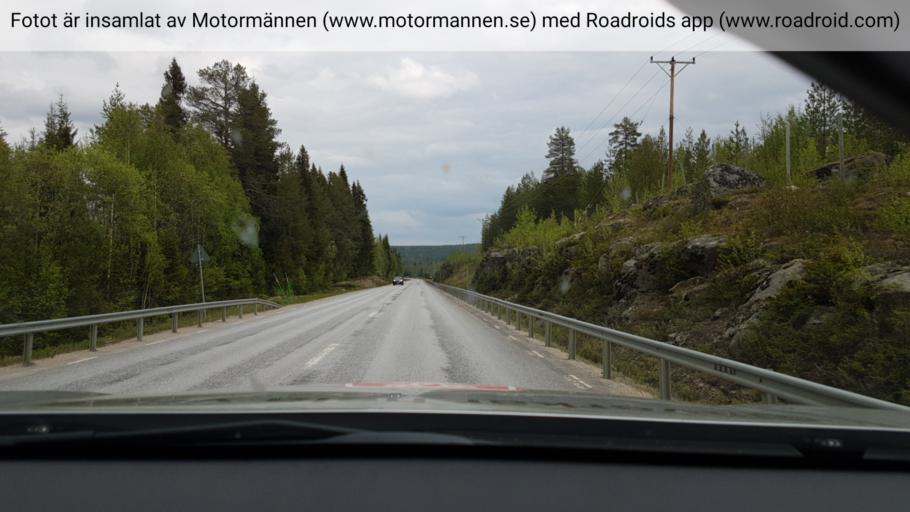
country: SE
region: Vaesterbotten
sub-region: Bjurholms Kommun
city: Bjurholm
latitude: 63.9297
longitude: 19.2734
